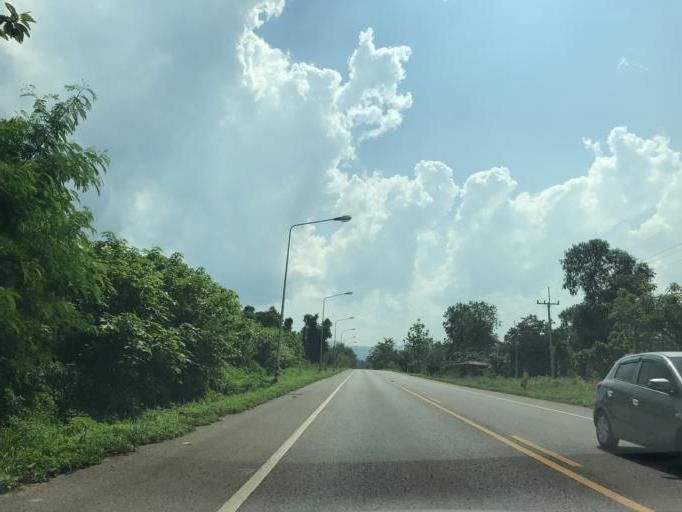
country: TH
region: Phayao
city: Phayao
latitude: 19.0862
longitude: 99.8929
